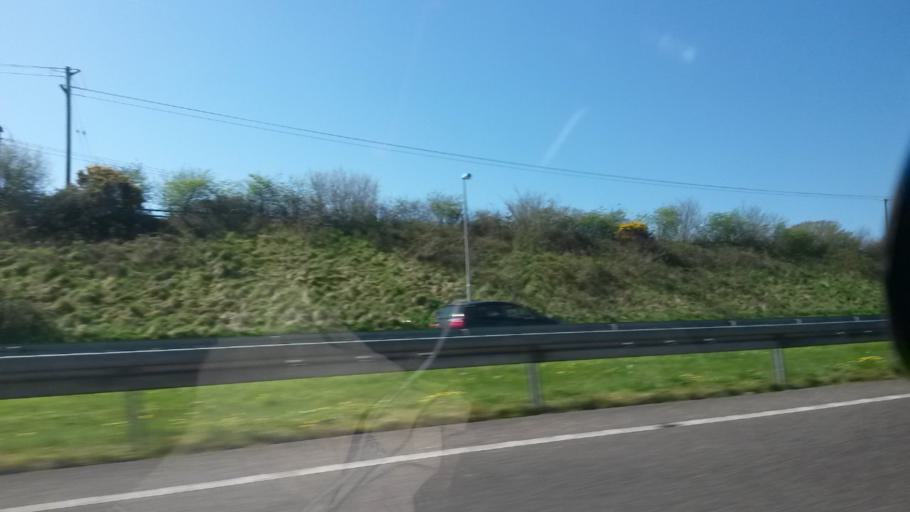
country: IE
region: Munster
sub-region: County Cork
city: Killumney
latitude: 51.8782
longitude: -8.6216
